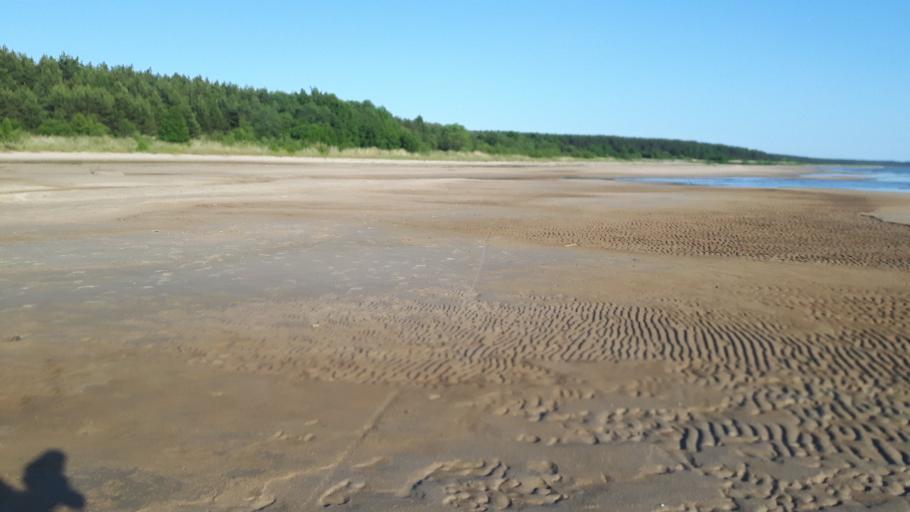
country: LV
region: Salacgrivas
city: Salacgriva
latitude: 57.6900
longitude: 24.3544
